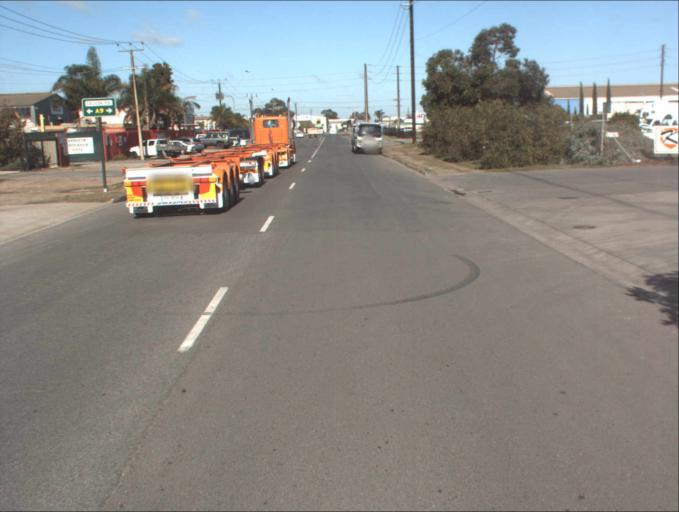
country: AU
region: South Australia
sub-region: Port Adelaide Enfield
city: Alberton
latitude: -34.8385
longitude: 138.5285
